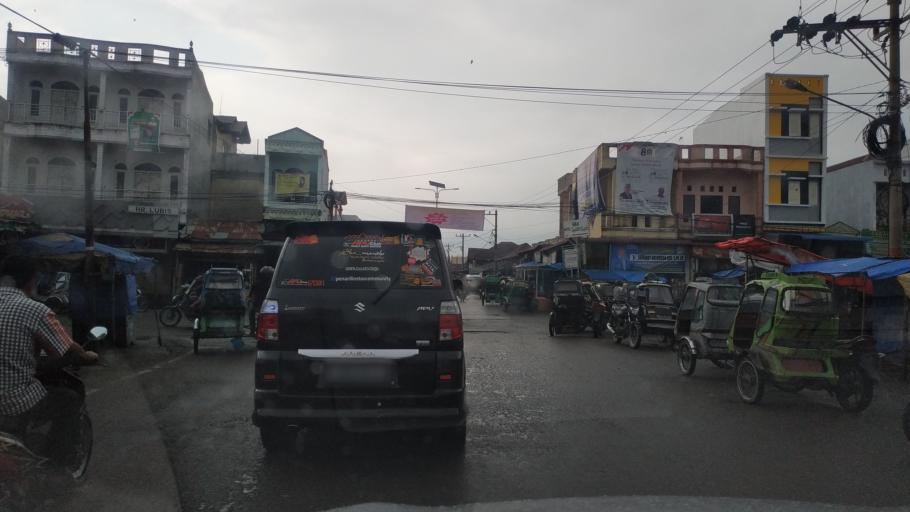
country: ID
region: North Sumatra
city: Sibubuhan
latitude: 1.0528
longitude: 99.7297
